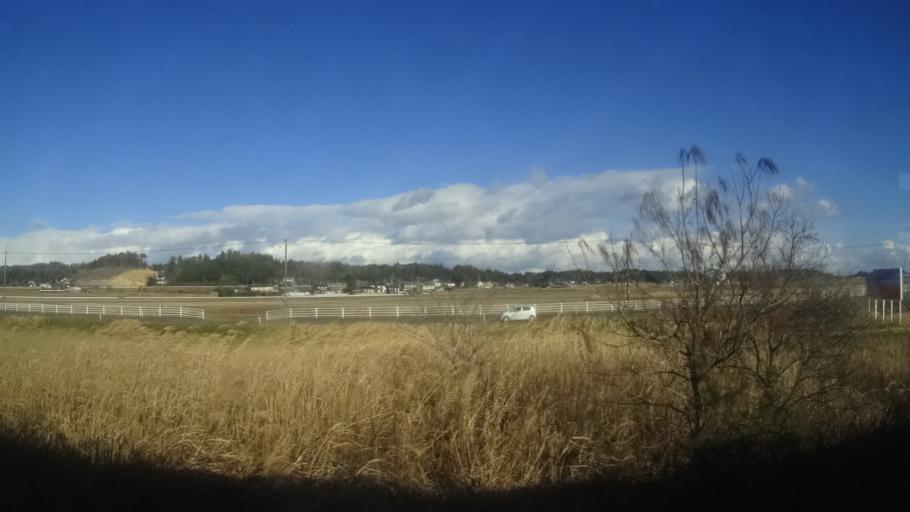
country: JP
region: Fukushima
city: Namie
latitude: 37.7099
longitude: 140.9638
